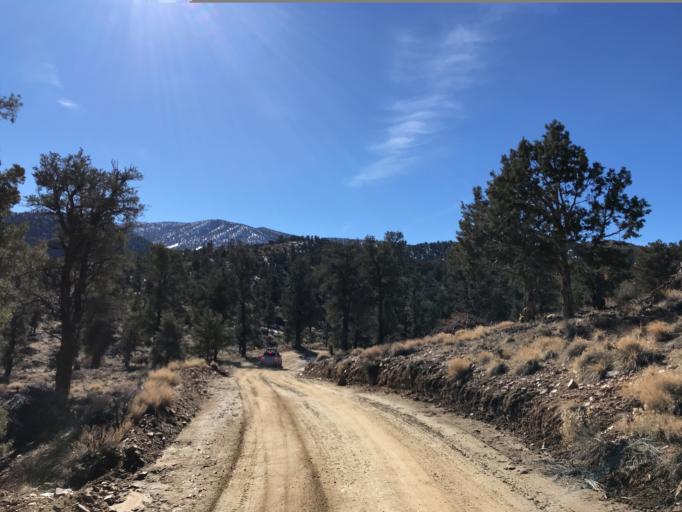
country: US
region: California
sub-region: San Bernardino County
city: Big Bear City
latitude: 34.2598
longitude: -116.7499
